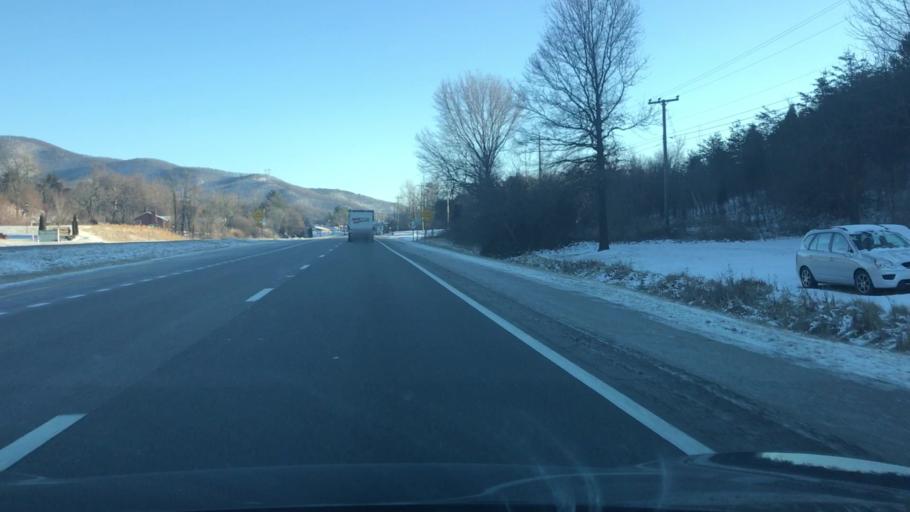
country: US
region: Virginia
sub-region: Botetourt County
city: Blue Ridge
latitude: 37.3789
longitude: -79.8062
